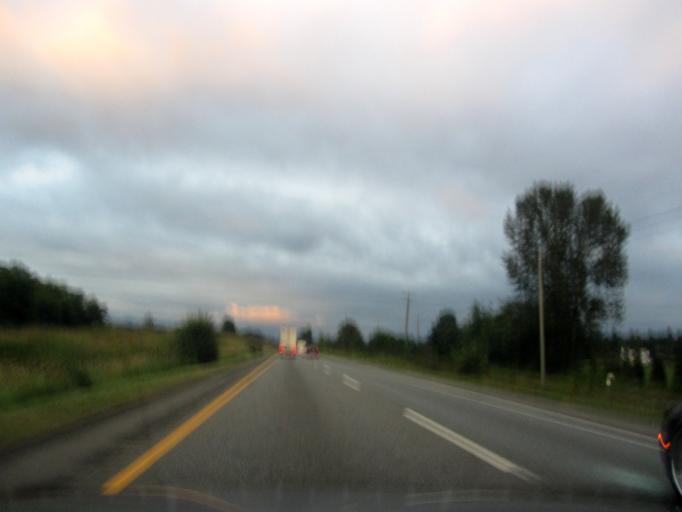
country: CA
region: British Columbia
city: Aldergrove
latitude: 49.0871
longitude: -122.4566
